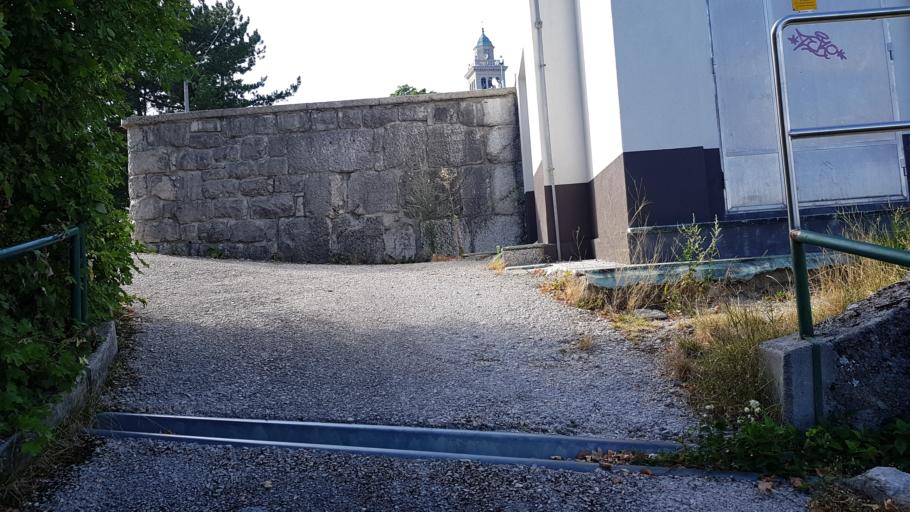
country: SI
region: Nova Gorica
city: Solkan
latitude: 45.9980
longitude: 13.6569
